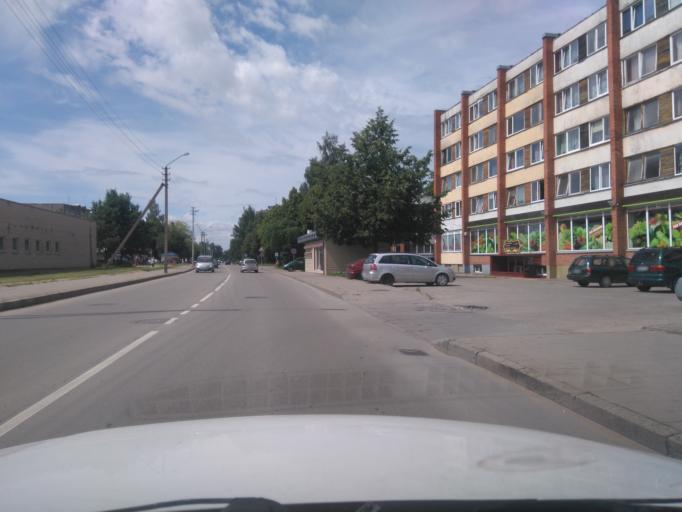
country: LT
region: Marijampoles apskritis
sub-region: Marijampole Municipality
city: Marijampole
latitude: 54.5682
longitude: 23.3572
